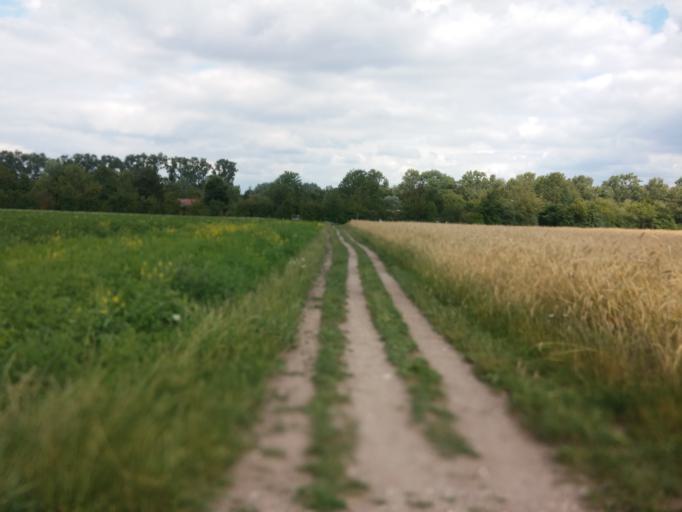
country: DE
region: Bavaria
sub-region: Upper Bavaria
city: Unterfoehring
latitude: 48.1512
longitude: 11.6625
